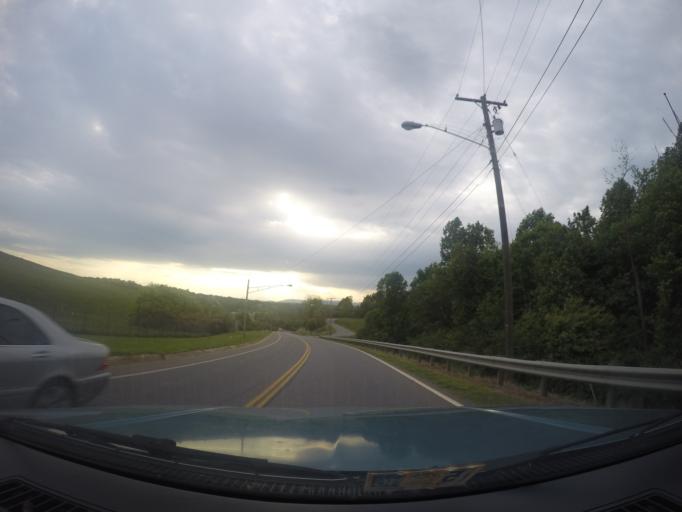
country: US
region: Virginia
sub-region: Amherst County
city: Madison Heights
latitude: 37.3942
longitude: -79.1048
